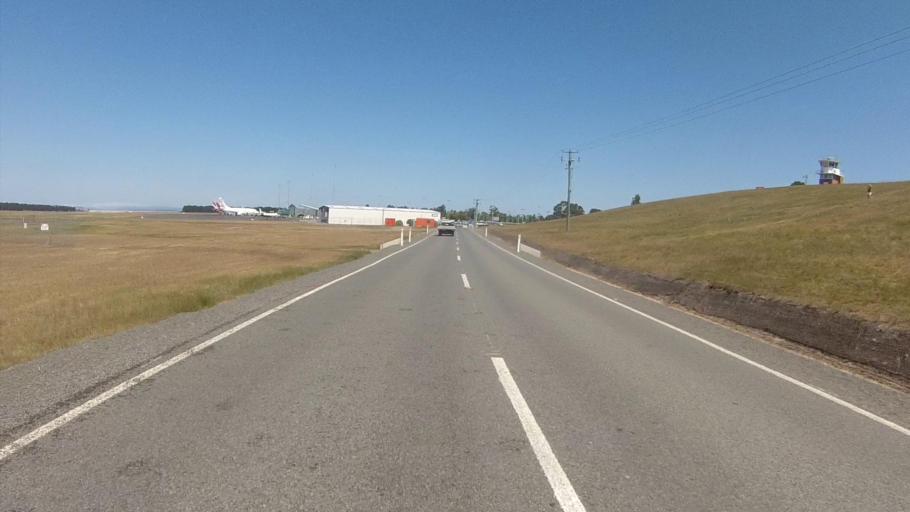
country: AU
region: Tasmania
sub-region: Clarence
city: Seven Mile Beach
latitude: -42.8337
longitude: 147.5025
